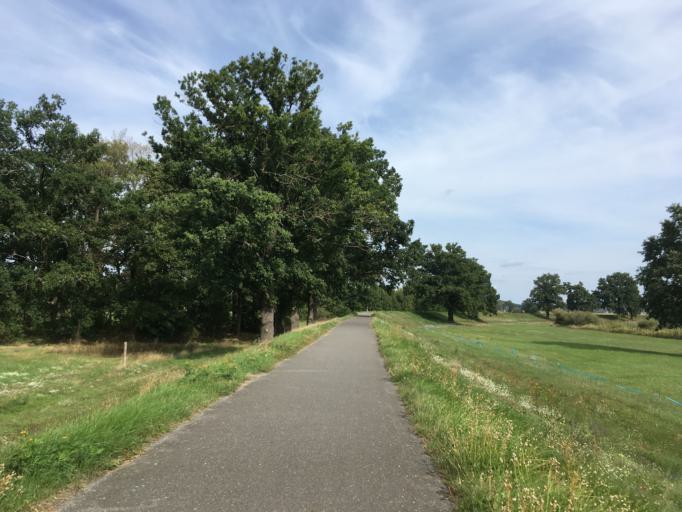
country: DE
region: Brandenburg
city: Schenkendobern
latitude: 51.8887
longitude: 14.6607
